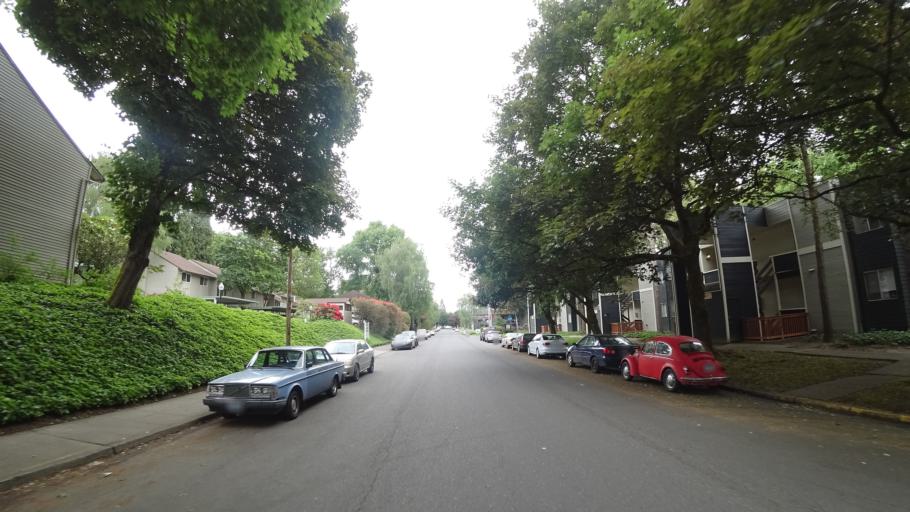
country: US
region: Oregon
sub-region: Clackamas County
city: Milwaukie
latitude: 45.4871
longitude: -122.6344
